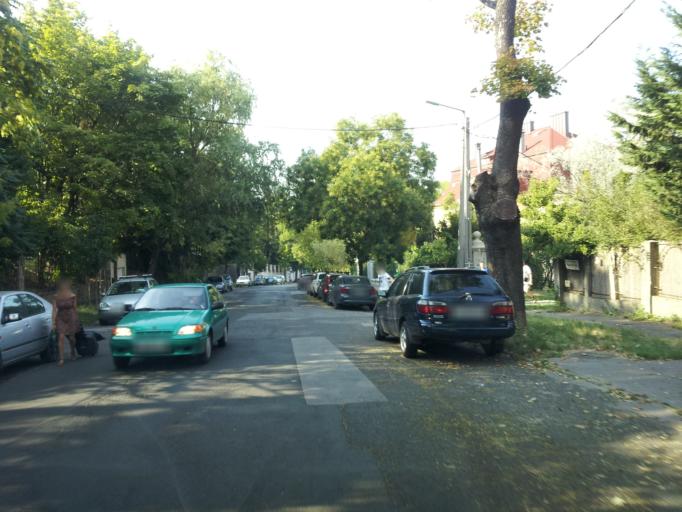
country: HU
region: Budapest
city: Budapest XII. keruelet
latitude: 47.5021
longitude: 19.0157
